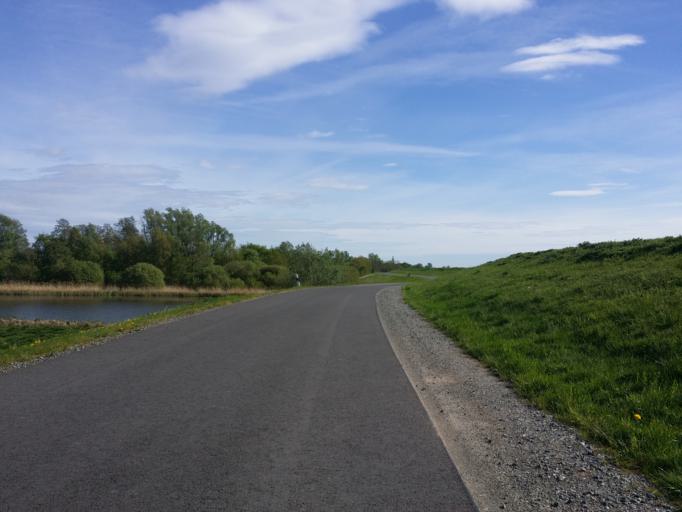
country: DE
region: Lower Saxony
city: Lemwerder
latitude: 53.1444
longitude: 8.6335
